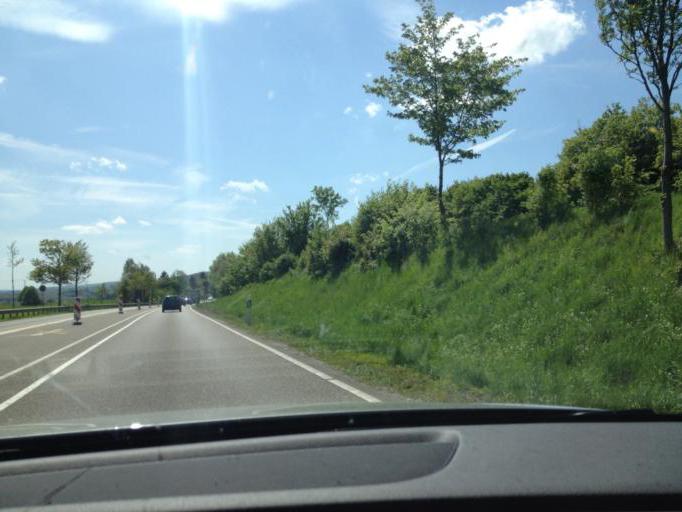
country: DE
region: North Rhine-Westphalia
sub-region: Regierungsbezirk Koln
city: Blankenheim
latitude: 50.4613
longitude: 6.6936
